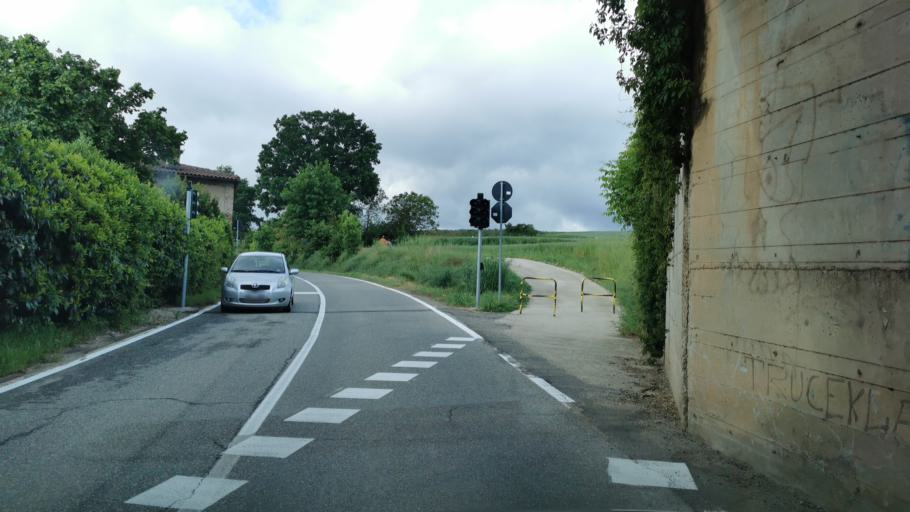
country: IT
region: Piedmont
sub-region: Provincia di Torino
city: Cambiano
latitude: 44.9939
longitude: 7.7821
